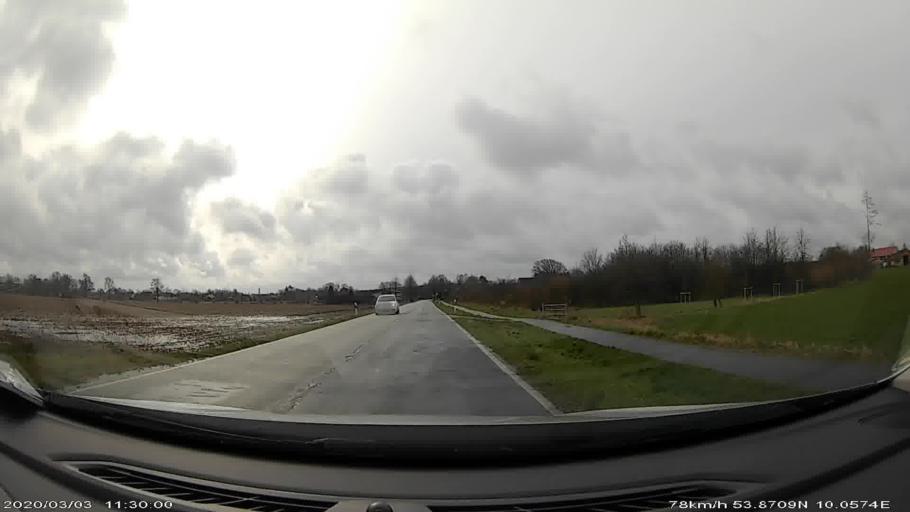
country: DE
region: Schleswig-Holstein
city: Struvenhutten
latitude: 53.8689
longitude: 10.0566
